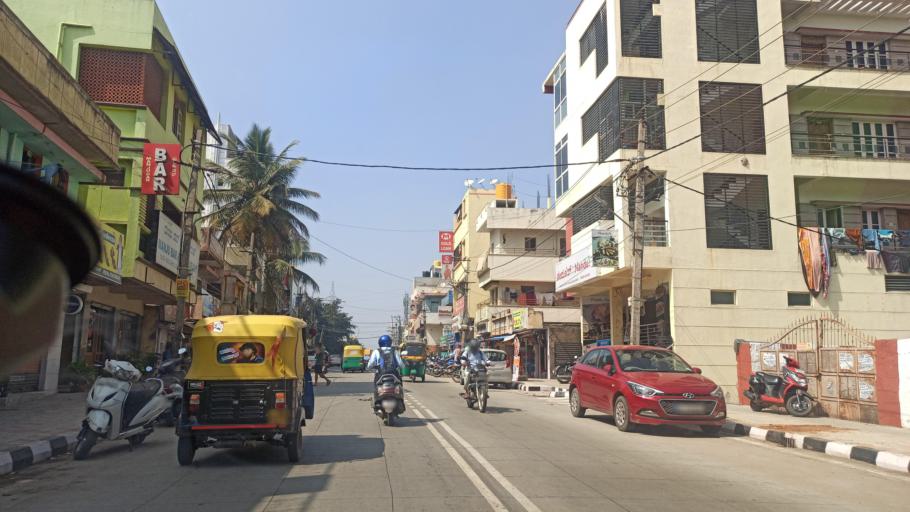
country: IN
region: Karnataka
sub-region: Bangalore Urban
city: Yelahanka
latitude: 13.0576
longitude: 77.5901
